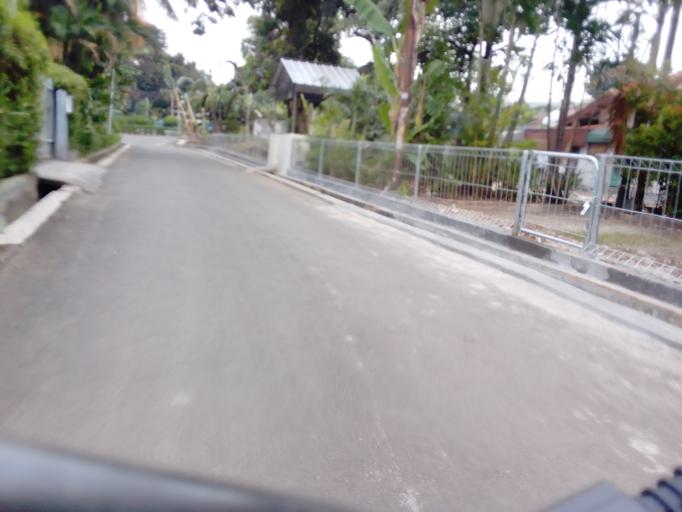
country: ID
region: Jakarta Raya
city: Jakarta
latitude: -6.2026
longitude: 106.8083
